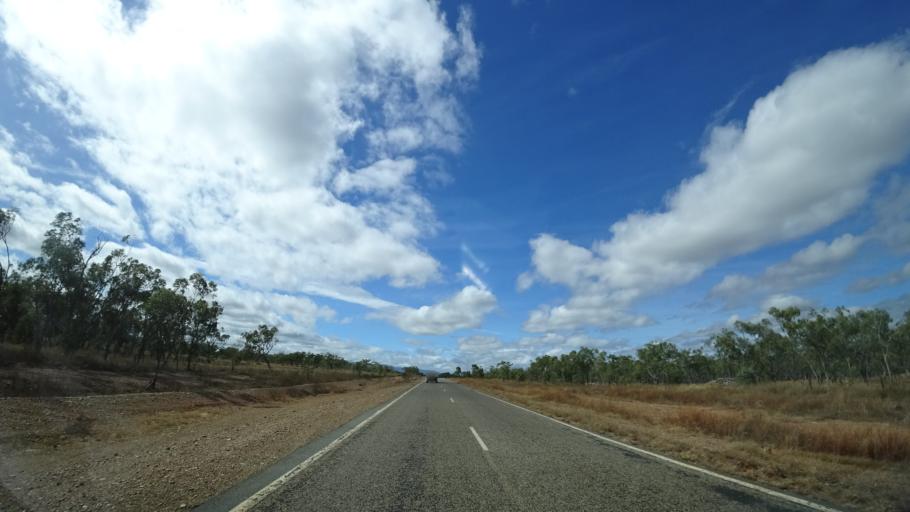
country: AU
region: Queensland
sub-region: Cairns
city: Port Douglas
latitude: -16.4961
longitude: 144.9701
